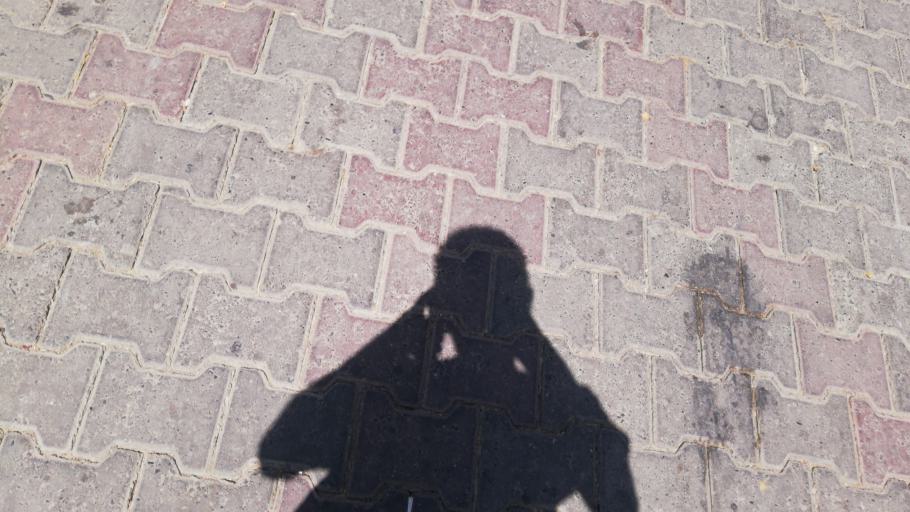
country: TR
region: Mardin
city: Midyat
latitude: 37.4160
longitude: 41.3754
